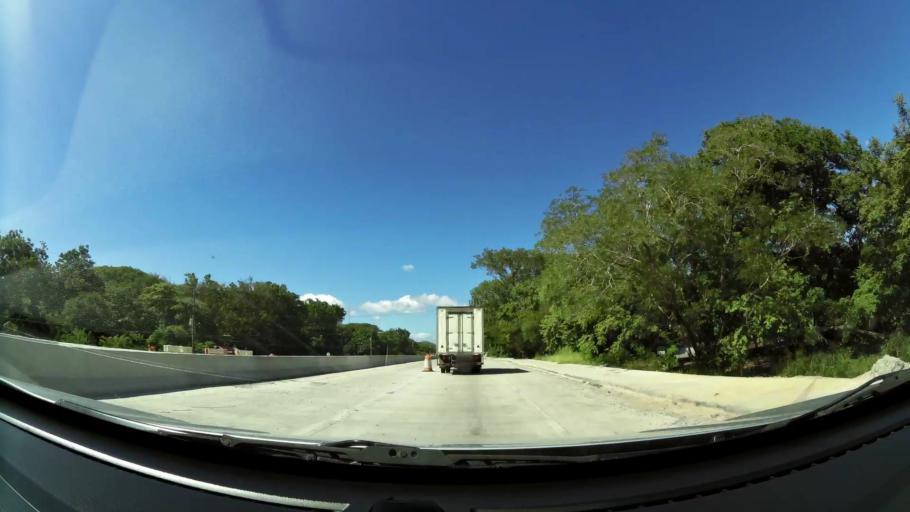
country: CR
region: Guanacaste
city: Liberia
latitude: 10.6042
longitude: -85.4290
